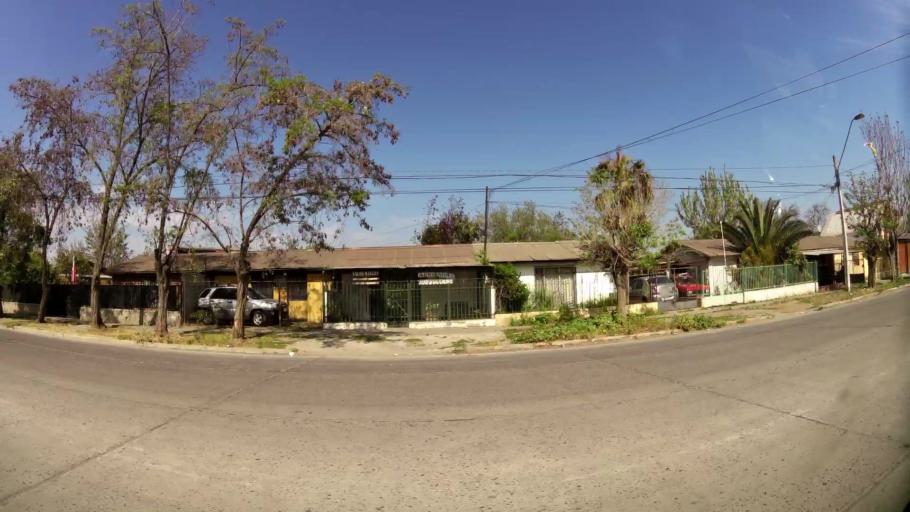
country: CL
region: Santiago Metropolitan
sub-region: Provincia de Santiago
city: Santiago
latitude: -33.3889
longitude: -70.6614
